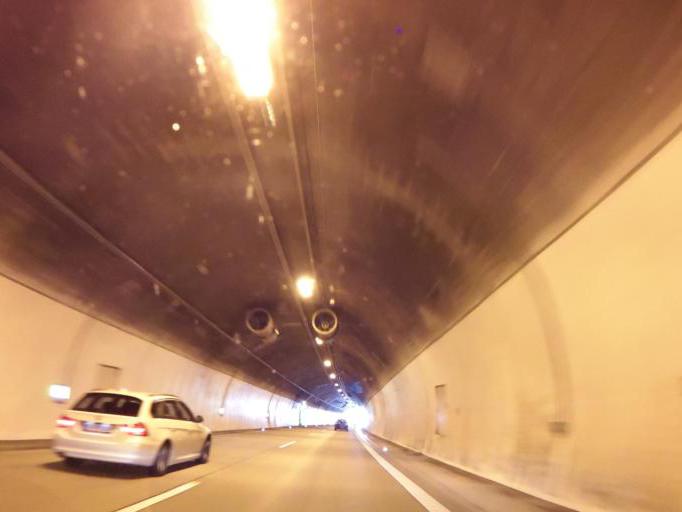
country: DE
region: Baden-Wuerttemberg
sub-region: Regierungsbezirk Stuttgart
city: Westhausen
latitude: 48.8738
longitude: 10.1682
